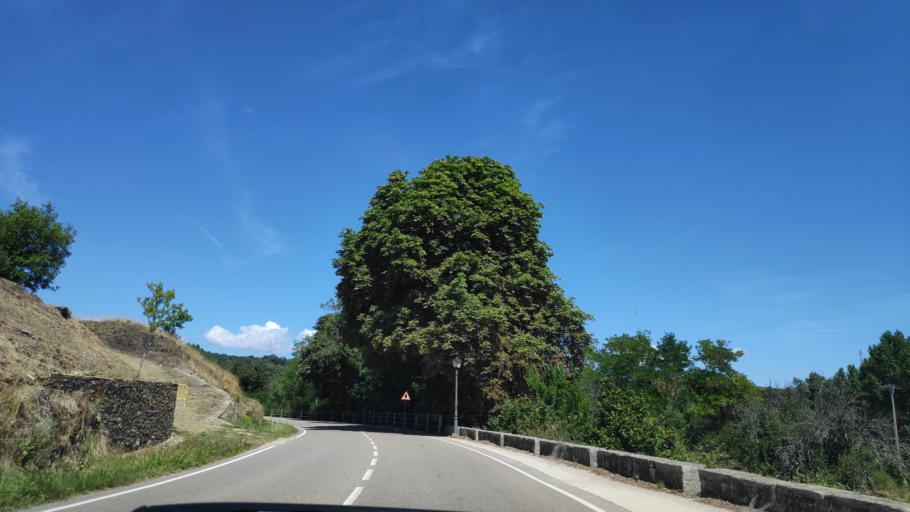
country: ES
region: Castille and Leon
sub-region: Provincia de Zamora
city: Puebla de Sanabria
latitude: 42.0565
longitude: -6.6331
